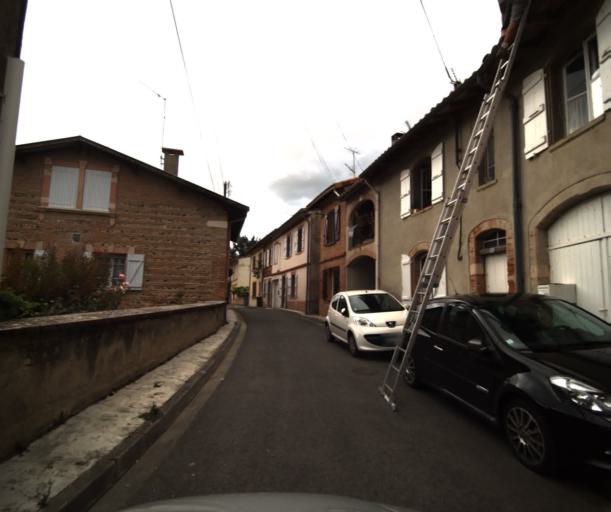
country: FR
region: Midi-Pyrenees
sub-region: Departement de la Haute-Garonne
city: Le Fauga
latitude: 43.4123
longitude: 1.3089
